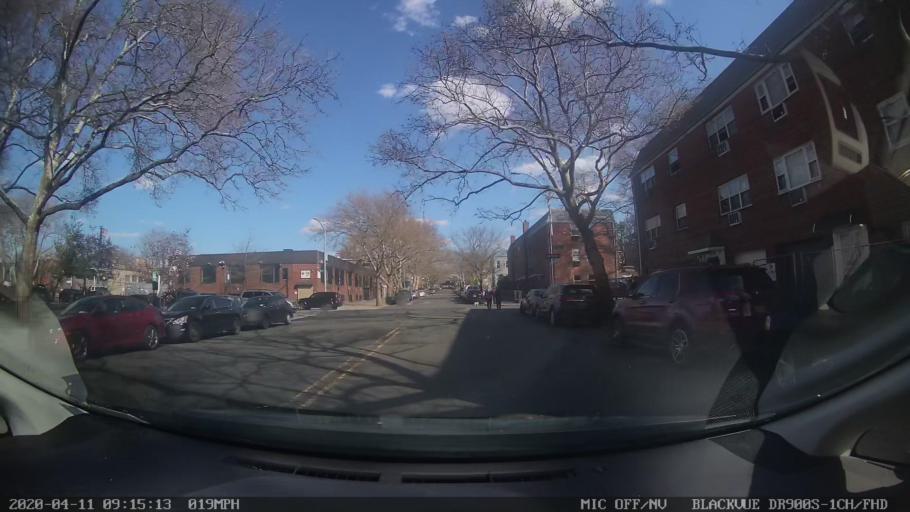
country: US
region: New York
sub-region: Queens County
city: Long Island City
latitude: 40.7589
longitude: -73.9347
